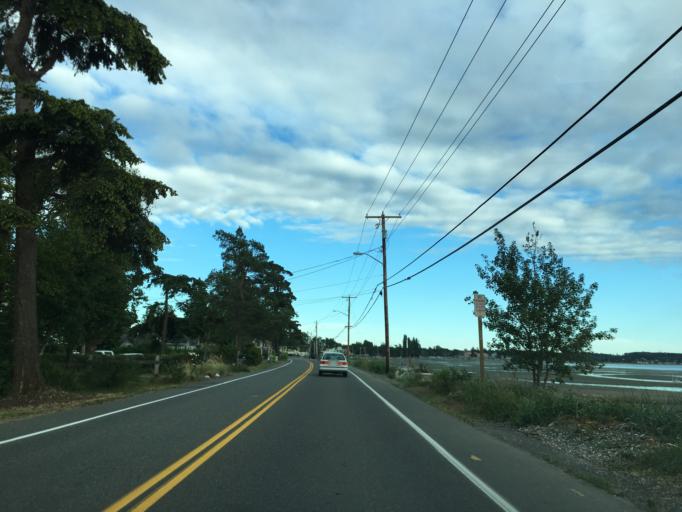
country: US
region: Washington
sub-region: Whatcom County
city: Birch Bay
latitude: 48.9384
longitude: -122.7547
